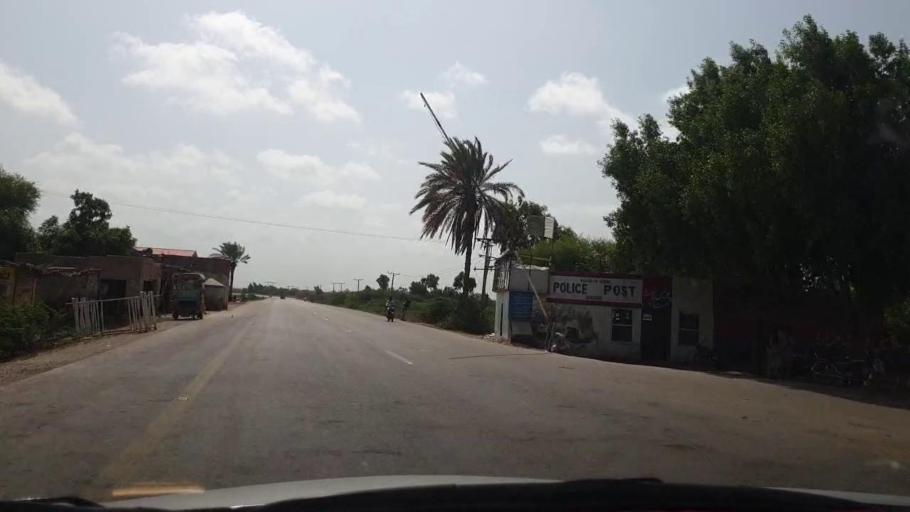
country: PK
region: Sindh
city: Talhar
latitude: 24.9132
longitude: 68.7302
